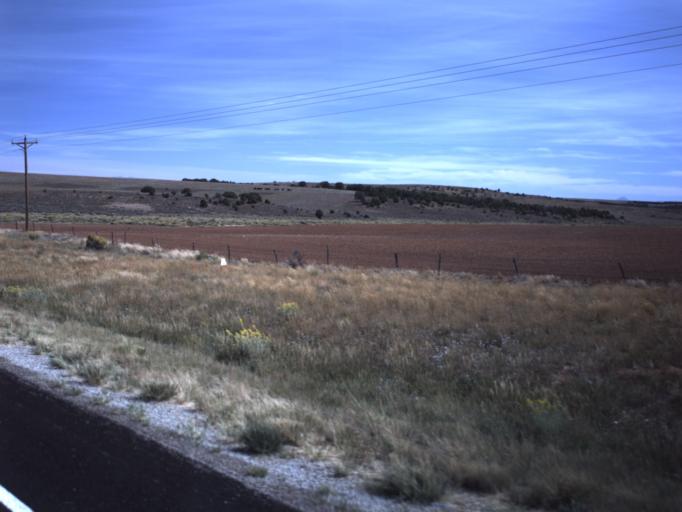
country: US
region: Utah
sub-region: San Juan County
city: Monticello
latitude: 37.8728
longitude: -109.3041
